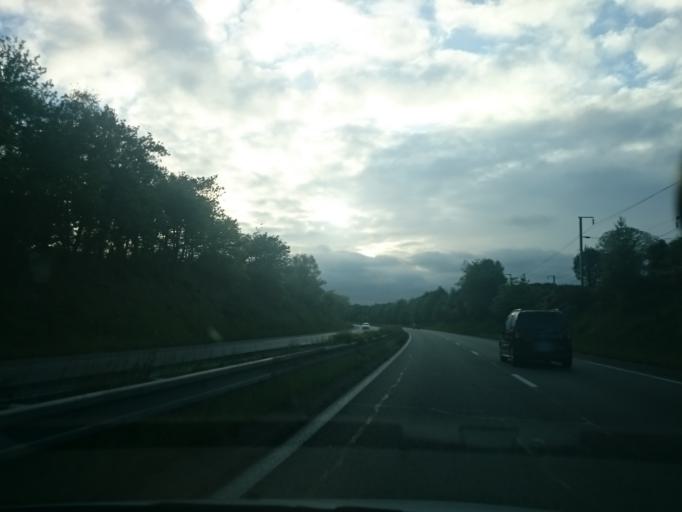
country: FR
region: Brittany
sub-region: Departement du Finistere
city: Quimperle
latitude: 47.8585
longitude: -3.5288
